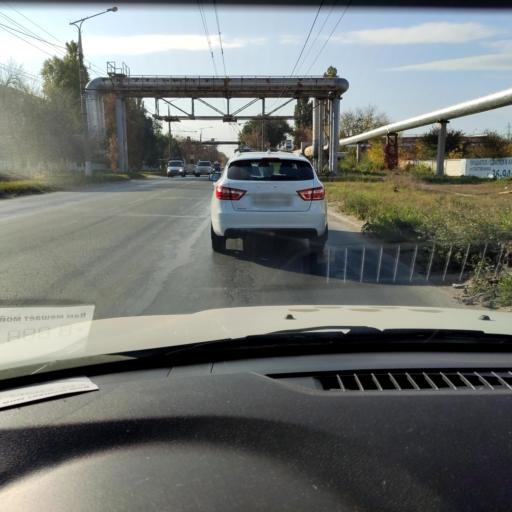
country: RU
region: Samara
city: Tol'yatti
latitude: 53.5454
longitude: 49.4458
